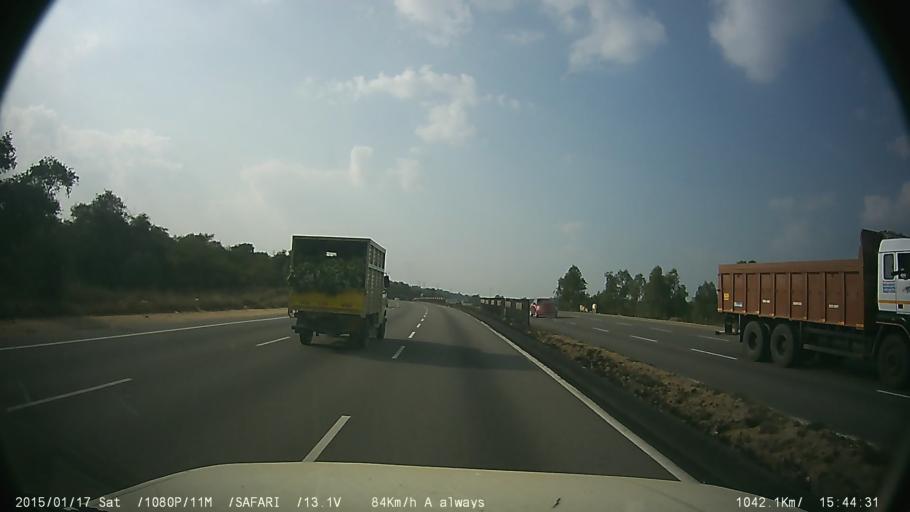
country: IN
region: Tamil Nadu
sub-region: Krishnagiri
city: Hosur
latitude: 12.6981
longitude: 77.9123
